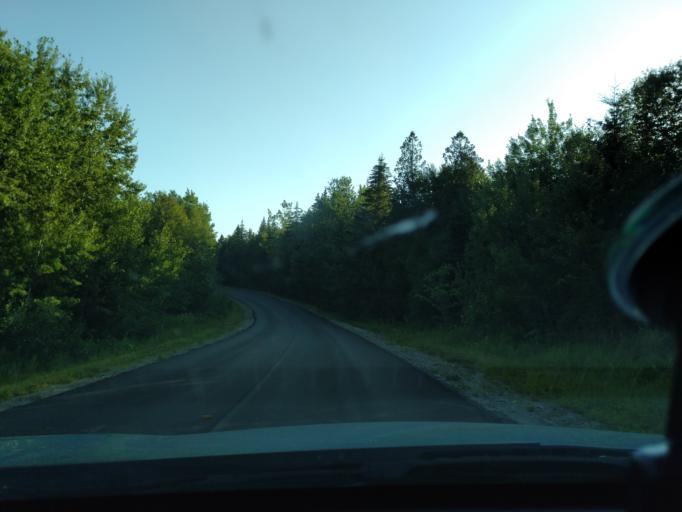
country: US
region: Maine
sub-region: Washington County
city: Eastport
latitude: 44.7109
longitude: -67.1429
